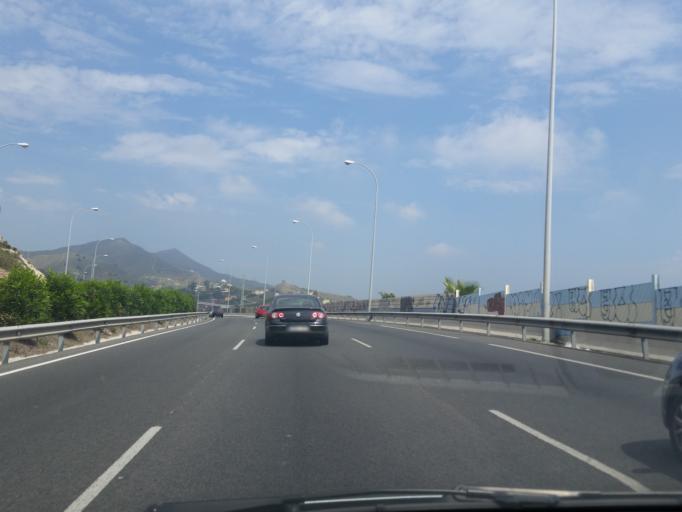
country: ES
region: Andalusia
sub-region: Provincia de Malaga
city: Malaga
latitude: 36.7331
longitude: -4.4539
